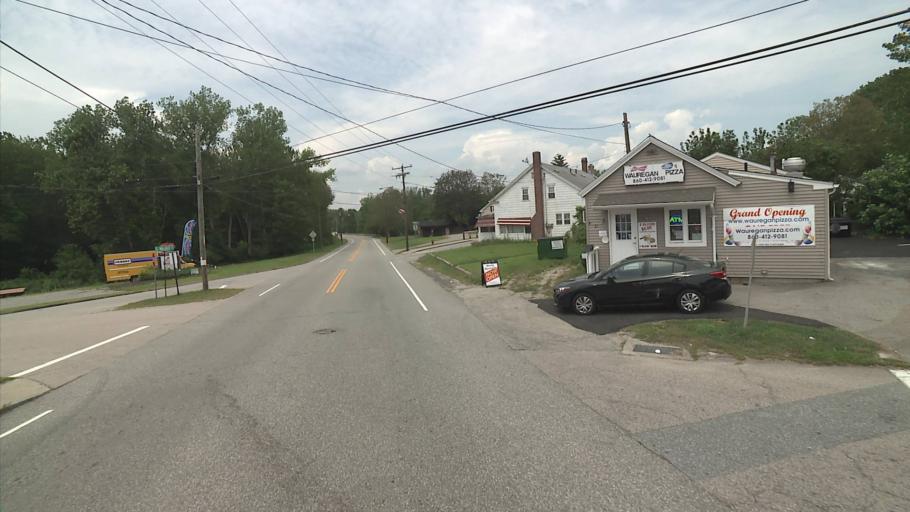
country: US
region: Connecticut
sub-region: Windham County
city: Wauregan
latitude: 41.7457
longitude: -71.9118
